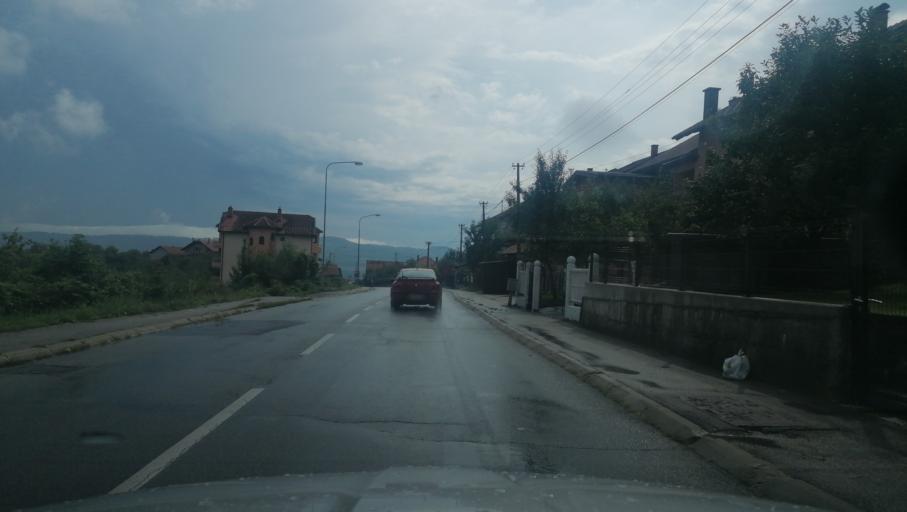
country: BA
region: Republika Srpska
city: Banja Luka
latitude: 44.7902
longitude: 17.1806
